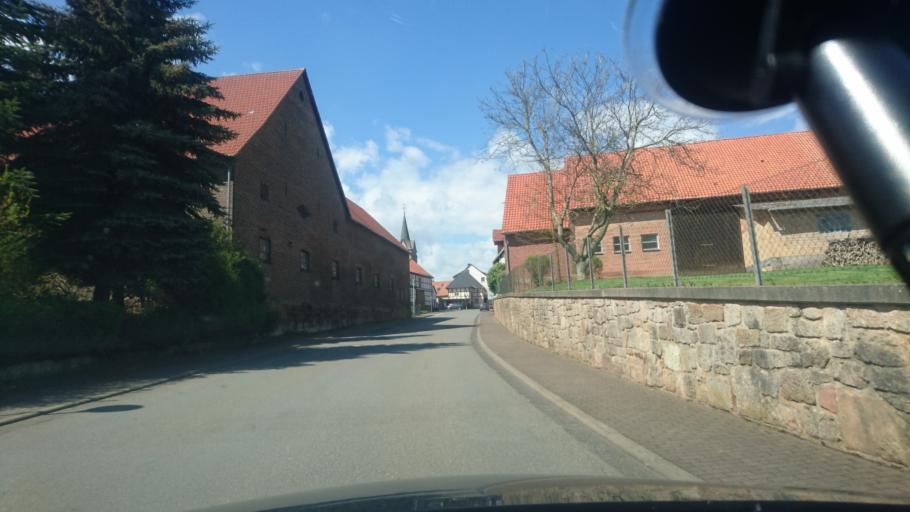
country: DE
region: North Rhine-Westphalia
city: Marsberg
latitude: 51.3852
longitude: 8.8953
